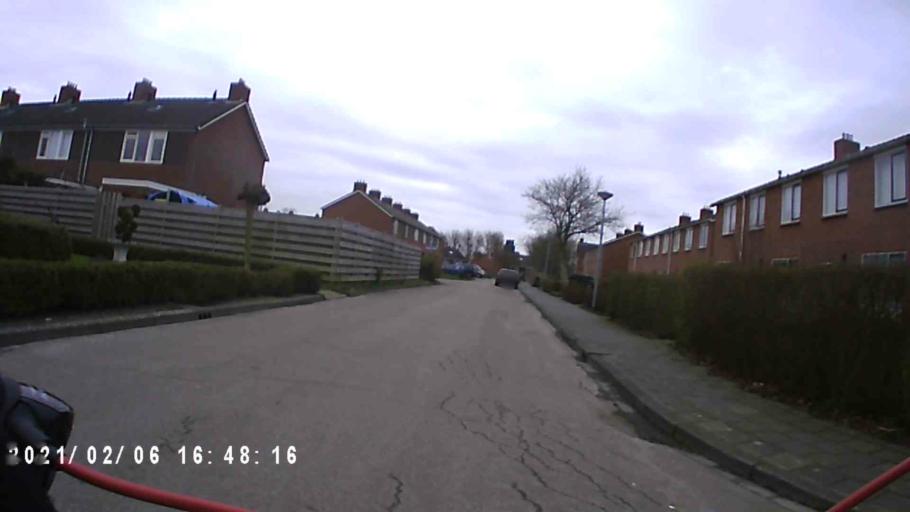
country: NL
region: Groningen
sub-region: Gemeente Appingedam
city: Appingedam
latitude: 53.4152
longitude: 6.7316
